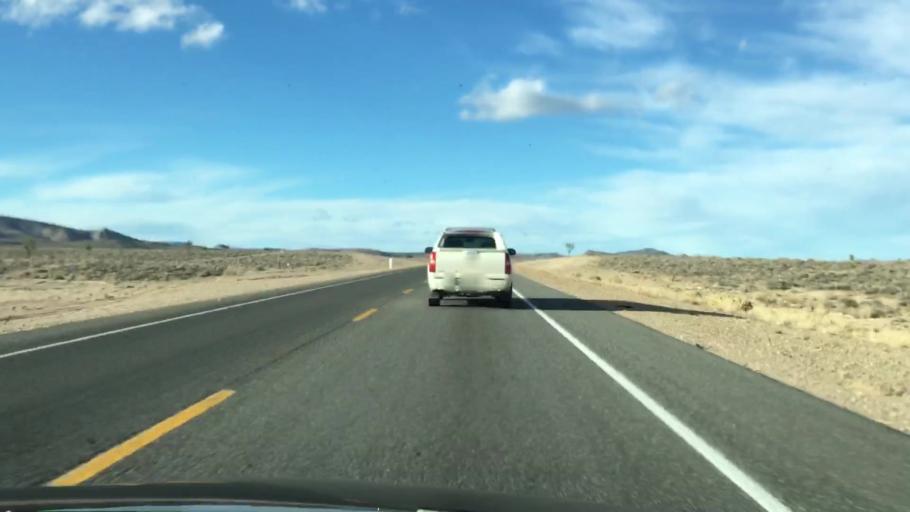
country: US
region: Nevada
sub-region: Esmeralda County
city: Goldfield
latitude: 37.5782
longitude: -117.2040
